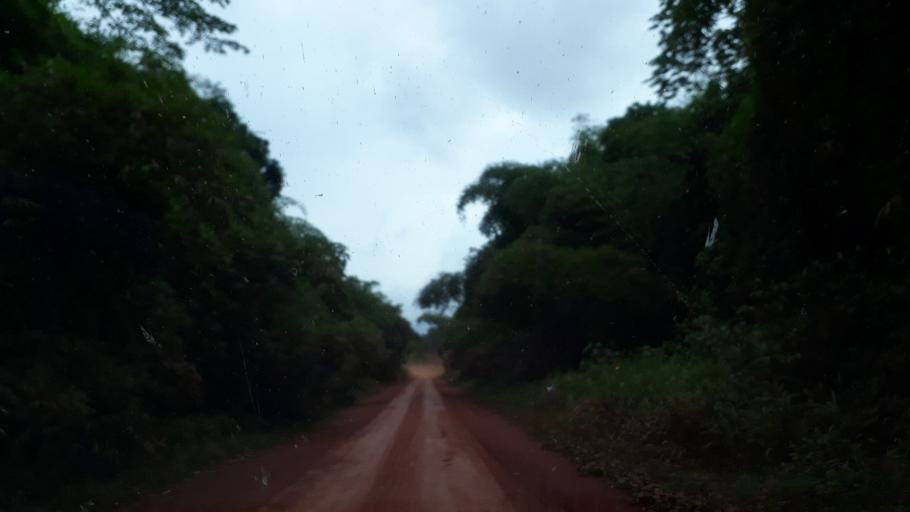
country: CD
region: Eastern Province
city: Kisangani
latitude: 0.5480
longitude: 25.8333
